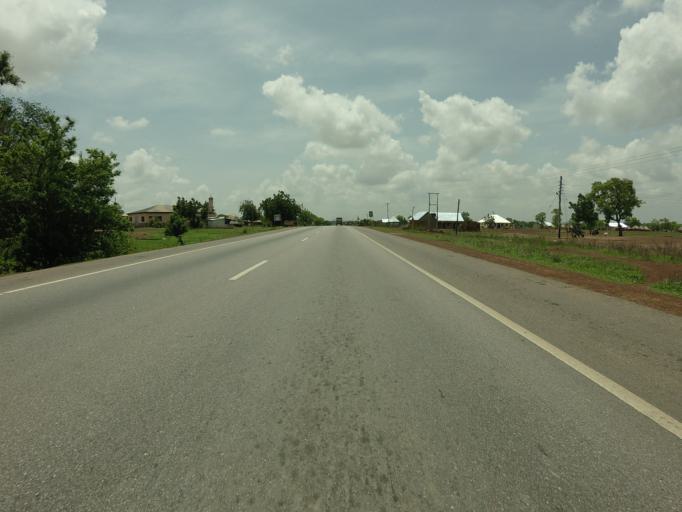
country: GH
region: Northern
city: Tamale
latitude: 9.2907
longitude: -0.9748
